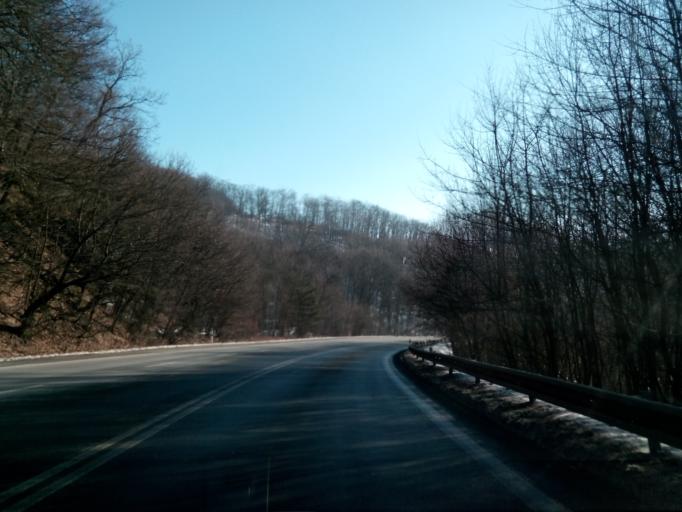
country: SK
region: Kosicky
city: Secovce
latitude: 48.7371
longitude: 21.5413
